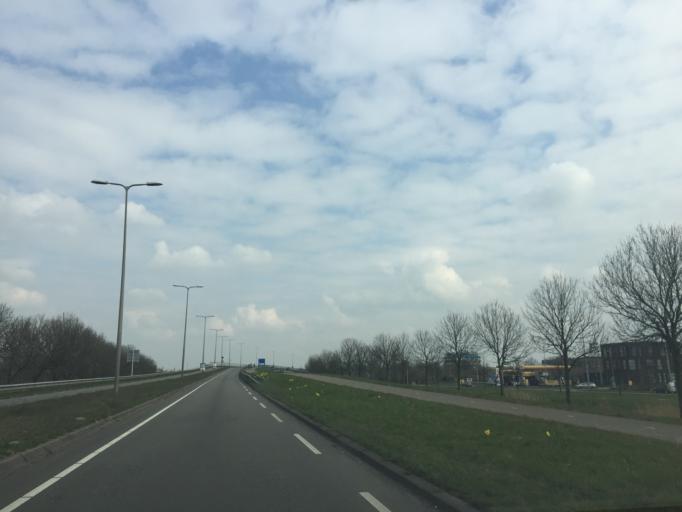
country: NL
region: South Holland
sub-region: Gemeente Alphen aan den Rijn
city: Alphen aan den Rijn
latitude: 52.1149
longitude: 4.6622
